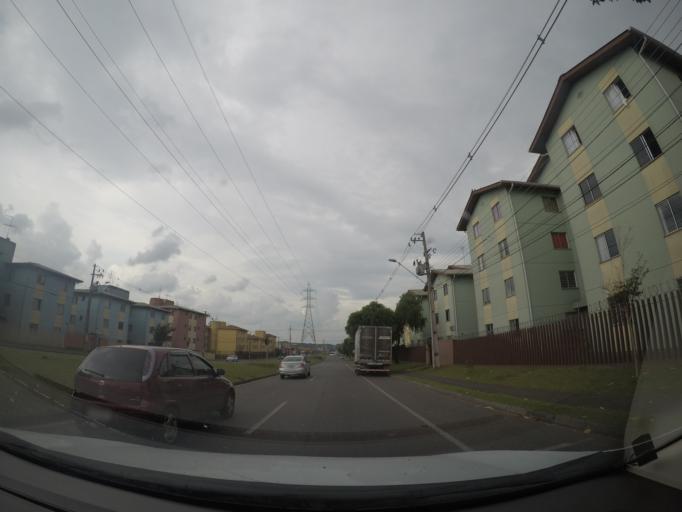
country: BR
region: Parana
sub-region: Sao Jose Dos Pinhais
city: Sao Jose dos Pinhais
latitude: -25.5482
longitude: -49.2597
